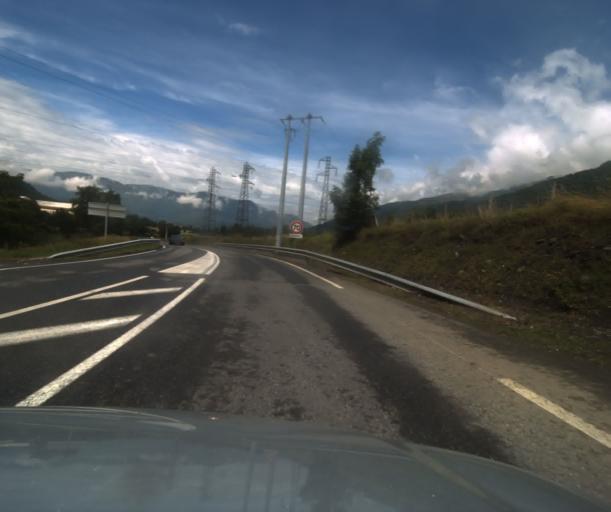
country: FR
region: Midi-Pyrenees
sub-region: Departement des Hautes-Pyrenees
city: Pierrefitte-Nestalas
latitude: 42.9542
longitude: -0.0649
